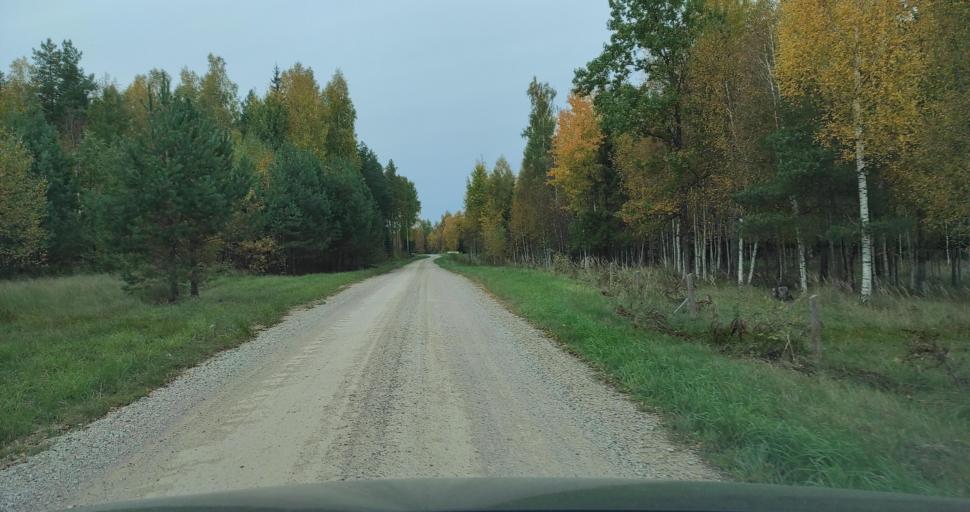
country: LV
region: Kuldigas Rajons
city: Kuldiga
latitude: 57.0238
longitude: 22.2000
